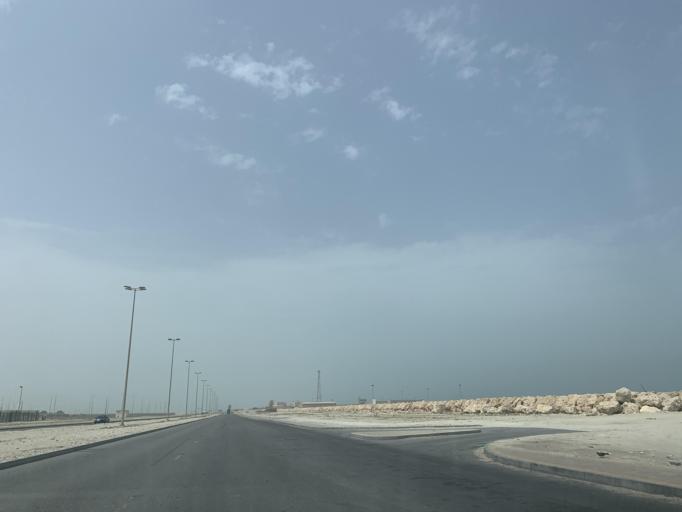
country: BH
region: Muharraq
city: Al Hadd
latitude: 26.2176
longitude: 50.7004
